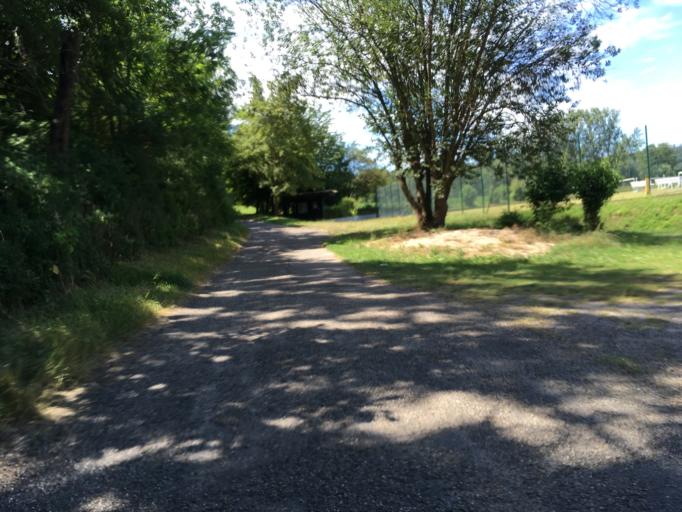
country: DE
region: Baden-Wuerttemberg
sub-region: Regierungsbezirk Stuttgart
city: Vaihingen an der Enz
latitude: 48.9176
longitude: 8.9725
